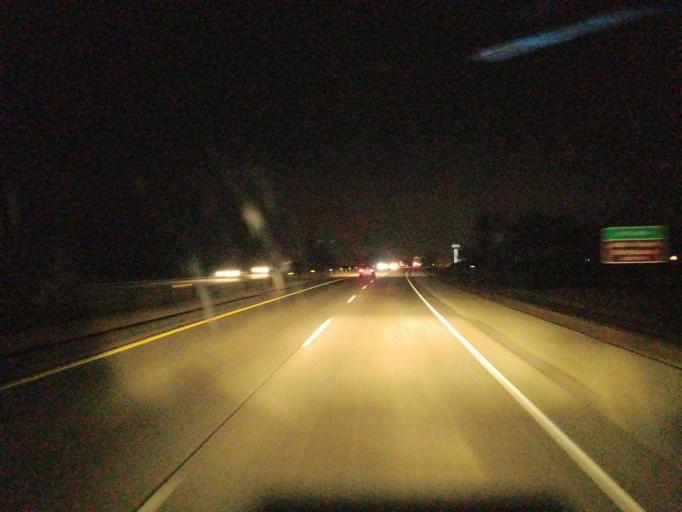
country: US
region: Iowa
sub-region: Dallas County
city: De Soto
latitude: 41.5377
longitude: -94.0289
